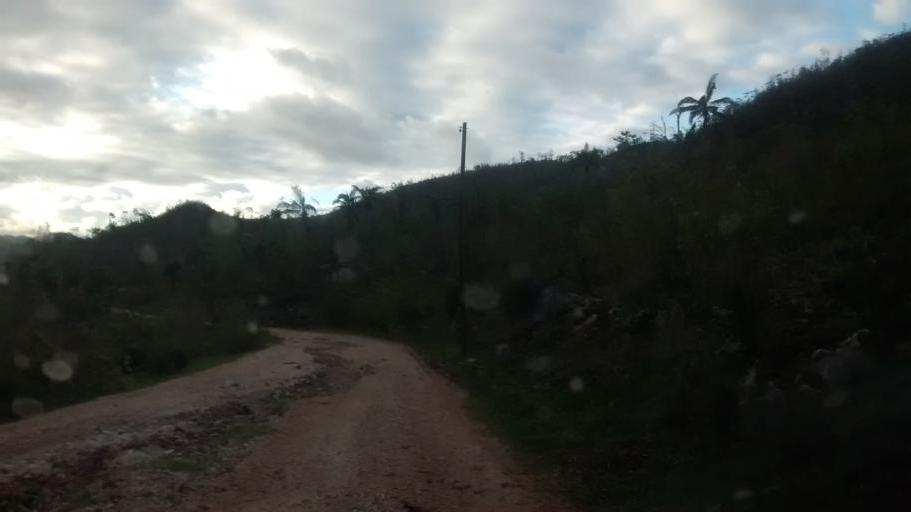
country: HT
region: Grandans
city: Corail
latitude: 18.4787
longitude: -73.8034
